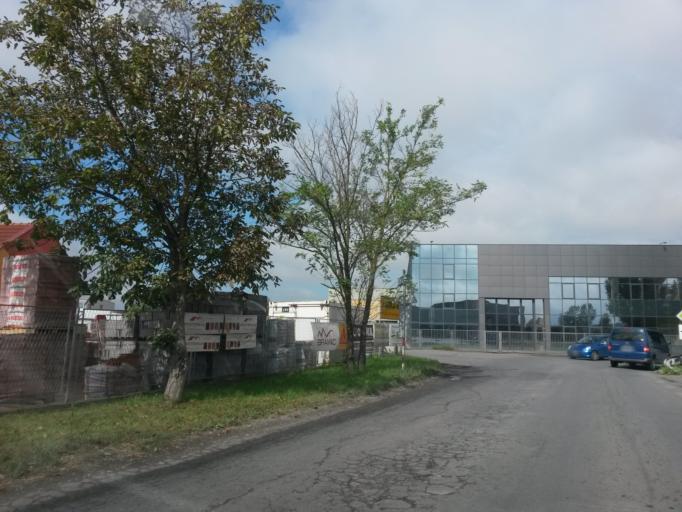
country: HR
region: Osjecko-Baranjska
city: Brijest
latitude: 45.5384
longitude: 18.6463
